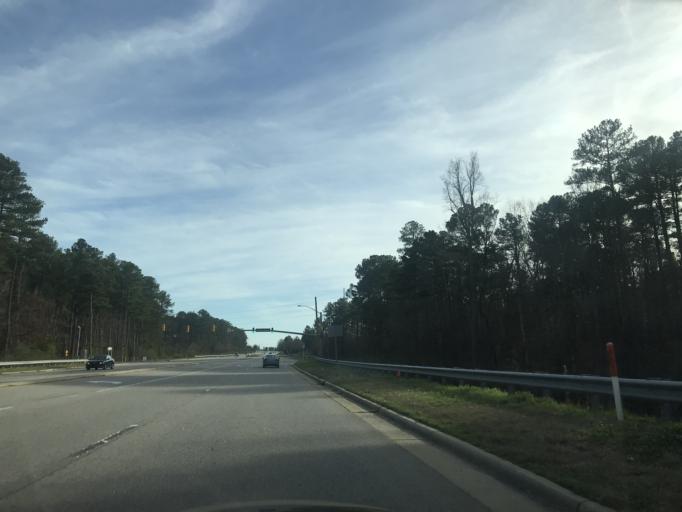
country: US
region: North Carolina
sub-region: Wake County
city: Morrisville
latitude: 35.8866
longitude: -78.8635
